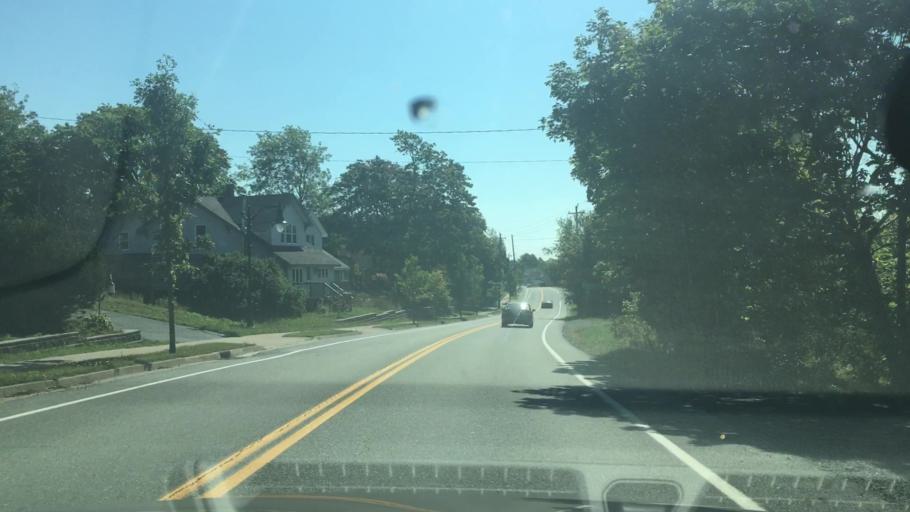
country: CA
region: Nova Scotia
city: New Glasgow
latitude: 44.9270
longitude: -62.5427
